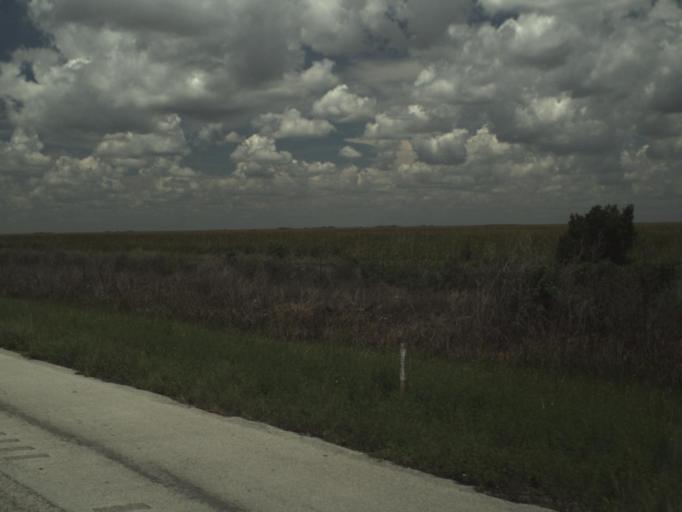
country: US
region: Florida
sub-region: Broward County
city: Weston
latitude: 26.1466
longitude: -80.6539
